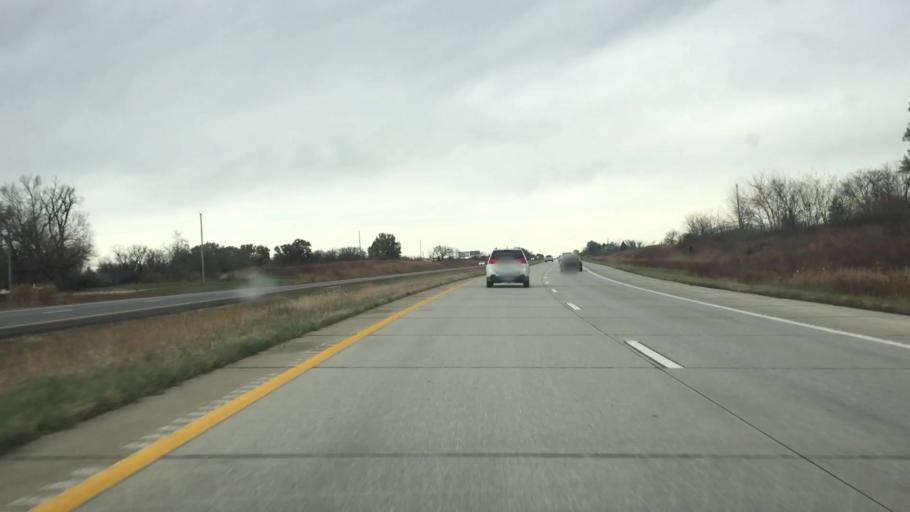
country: US
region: Missouri
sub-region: Saint Clair County
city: Osceola
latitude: 38.0882
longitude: -93.7076
